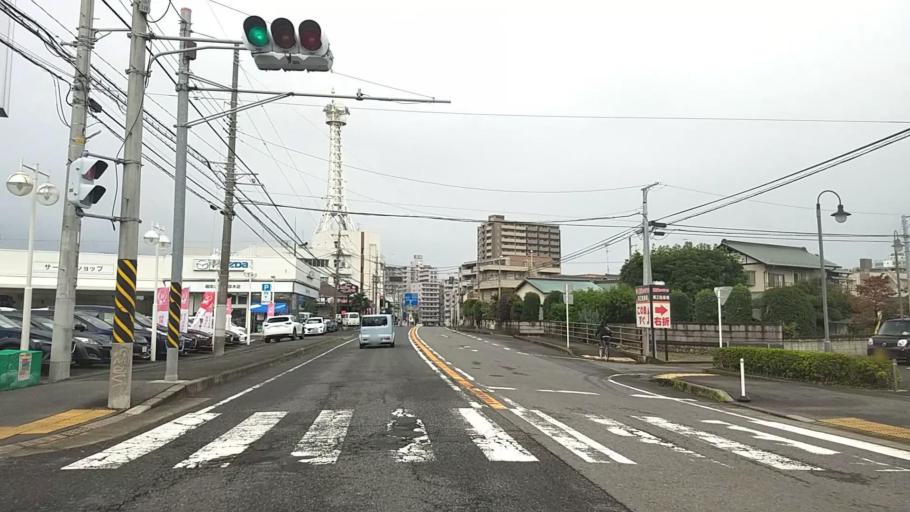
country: JP
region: Kanagawa
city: Atsugi
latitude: 35.4411
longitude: 139.3542
